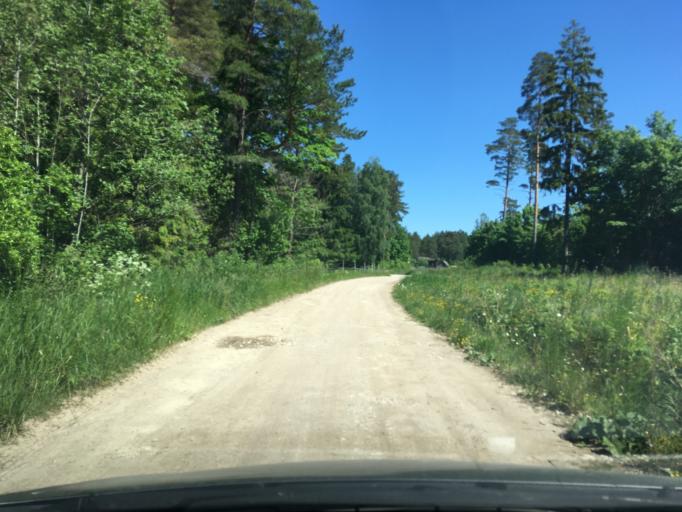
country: EE
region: Harju
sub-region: Raasiku vald
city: Raasiku
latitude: 59.1623
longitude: 25.1630
